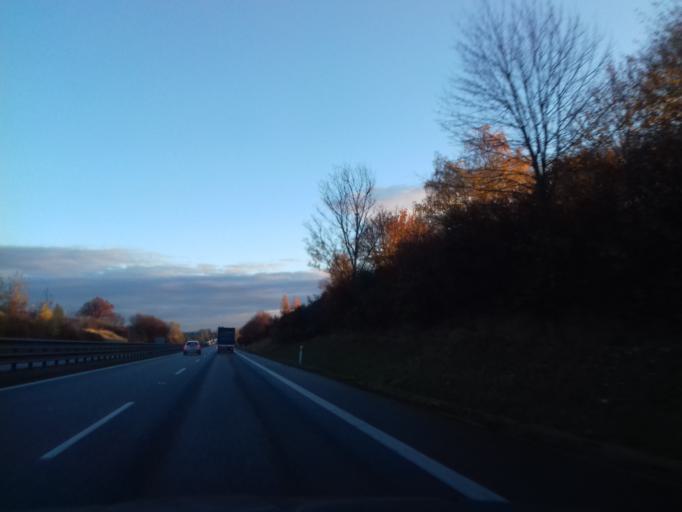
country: CZ
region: South Moravian
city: Pustimer
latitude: 49.3188
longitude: 17.0395
